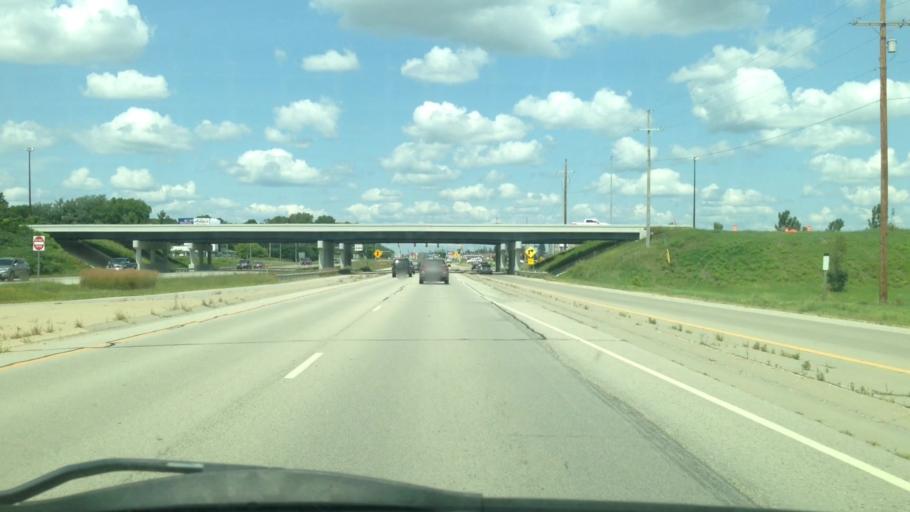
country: US
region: Minnesota
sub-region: Olmsted County
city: Rochester
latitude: 43.9751
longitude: -92.4626
